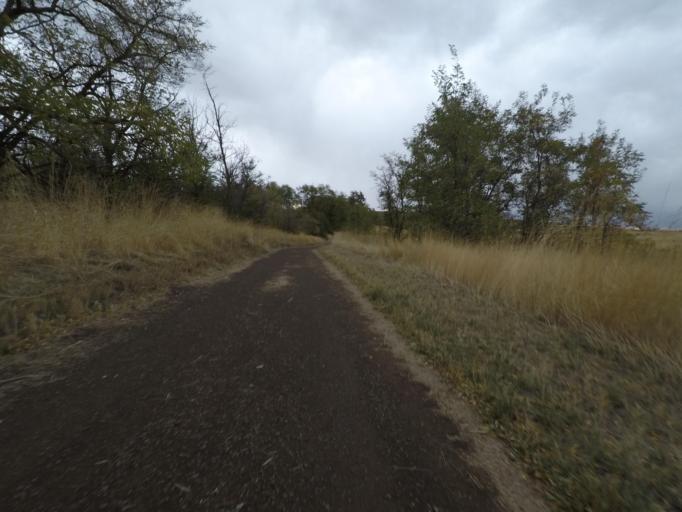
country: US
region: Washington
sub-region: Walla Walla County
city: Walla Walla East
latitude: 46.0625
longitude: -118.2565
